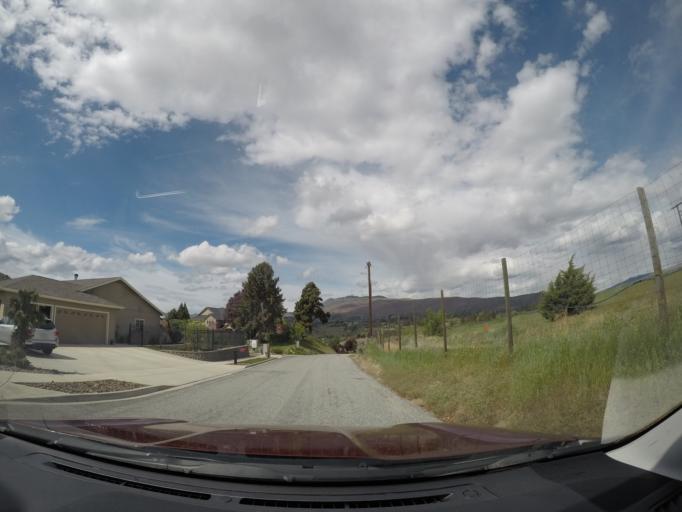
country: US
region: Washington
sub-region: Chelan County
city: Sunnyslope
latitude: 47.4584
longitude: -120.3435
